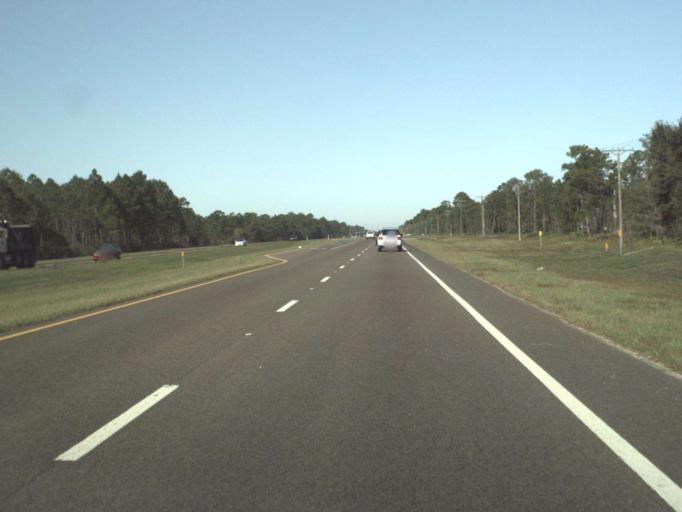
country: US
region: Florida
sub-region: Walton County
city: Seaside
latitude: 30.3628
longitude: -86.1688
